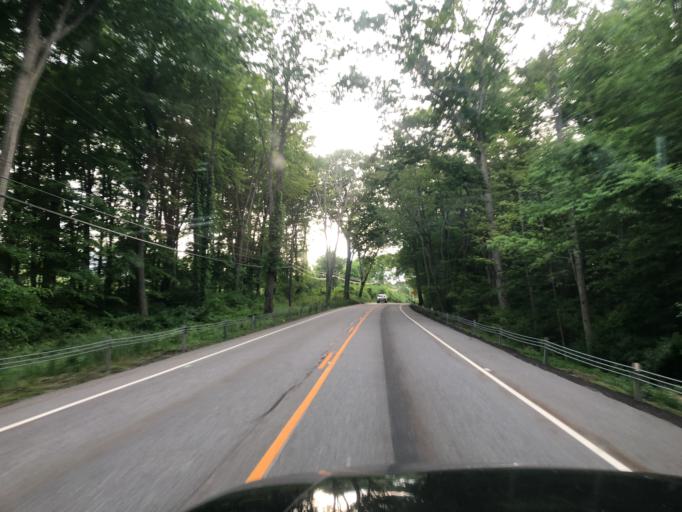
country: US
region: Connecticut
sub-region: Tolland County
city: Storrs
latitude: 41.8725
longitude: -72.2185
